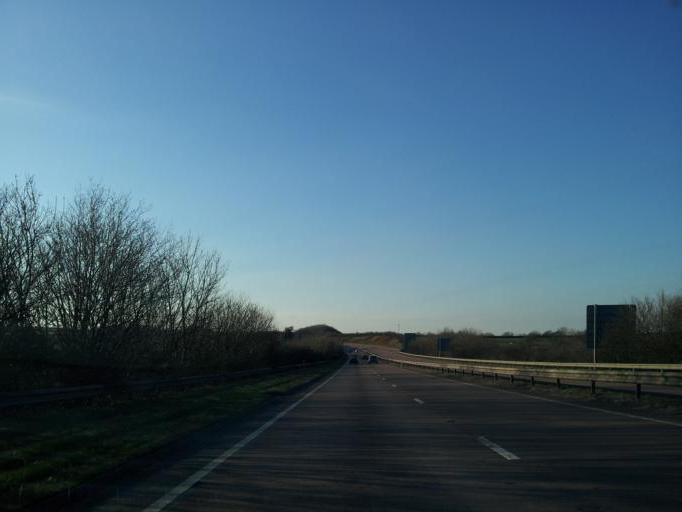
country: GB
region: England
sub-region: Devon
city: Okehampton
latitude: 50.7242
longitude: -3.8532
